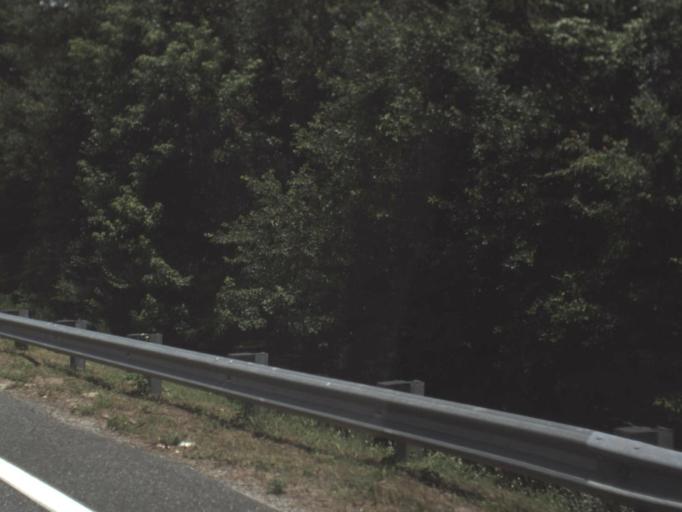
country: US
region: Florida
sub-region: Lafayette County
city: Mayo
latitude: 30.1073
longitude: -83.1710
